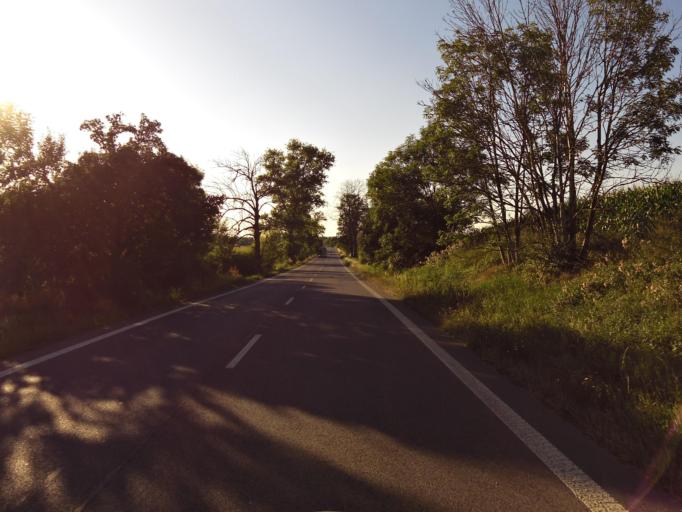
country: CZ
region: Central Bohemia
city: Mnichovo Hradiste
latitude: 50.5129
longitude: 14.9967
